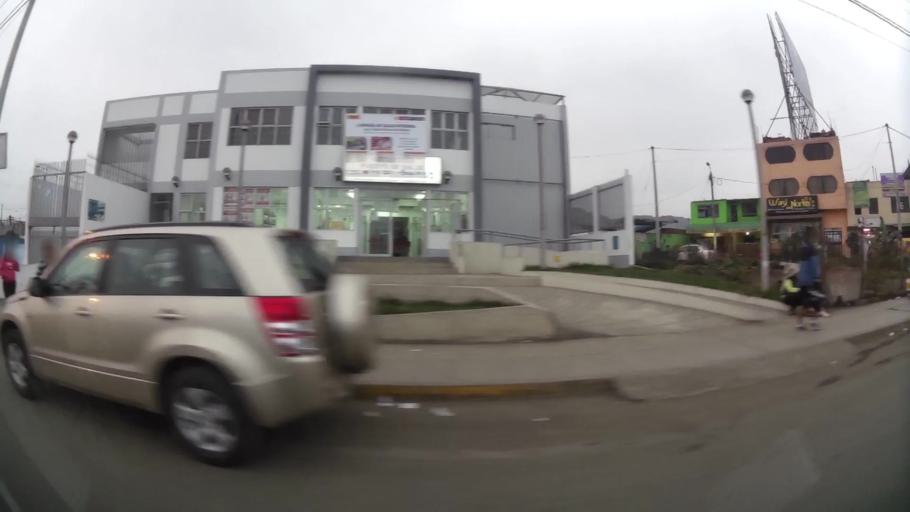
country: PE
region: Lima
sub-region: Lima
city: Surco
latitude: -12.1487
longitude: -76.9818
